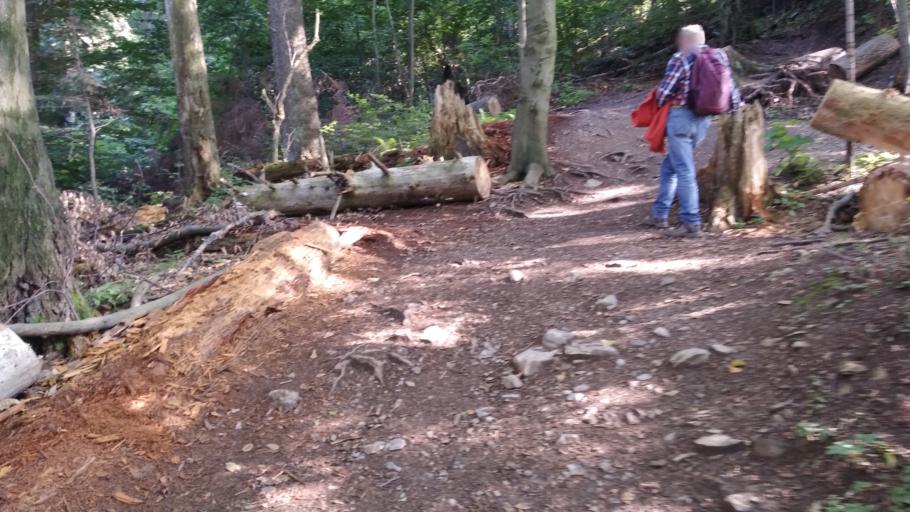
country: PL
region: Lesser Poland Voivodeship
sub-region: Powiat nowotarski
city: Kroscienko nad Dunajcem
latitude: 49.4190
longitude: 20.4398
